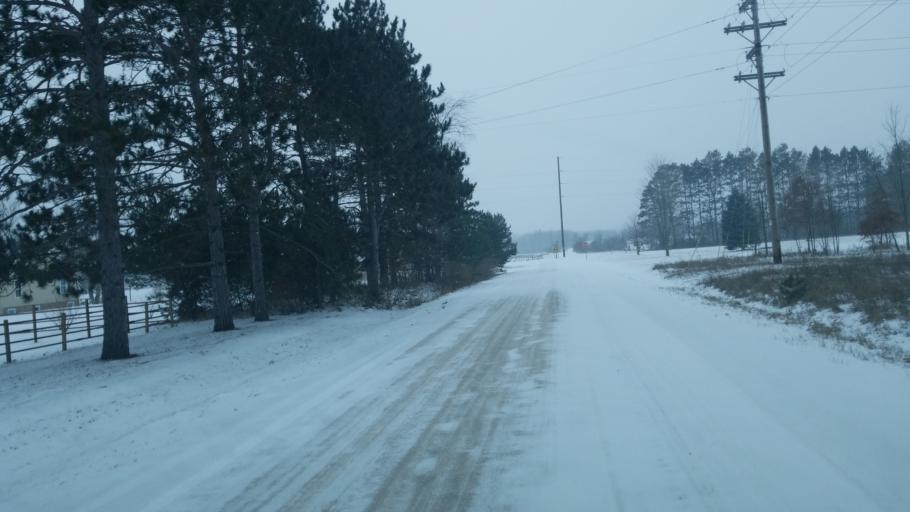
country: US
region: Michigan
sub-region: Osceola County
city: Reed City
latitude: 43.8291
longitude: -85.4223
